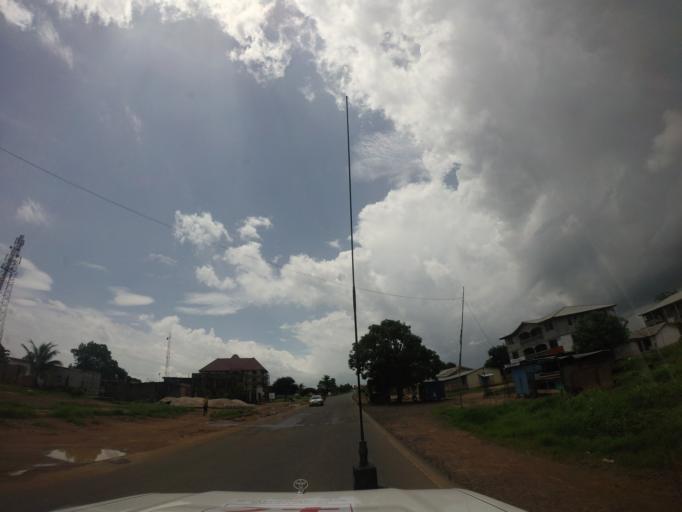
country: SL
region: Western Area
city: Waterloo
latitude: 8.3347
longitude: -13.0399
